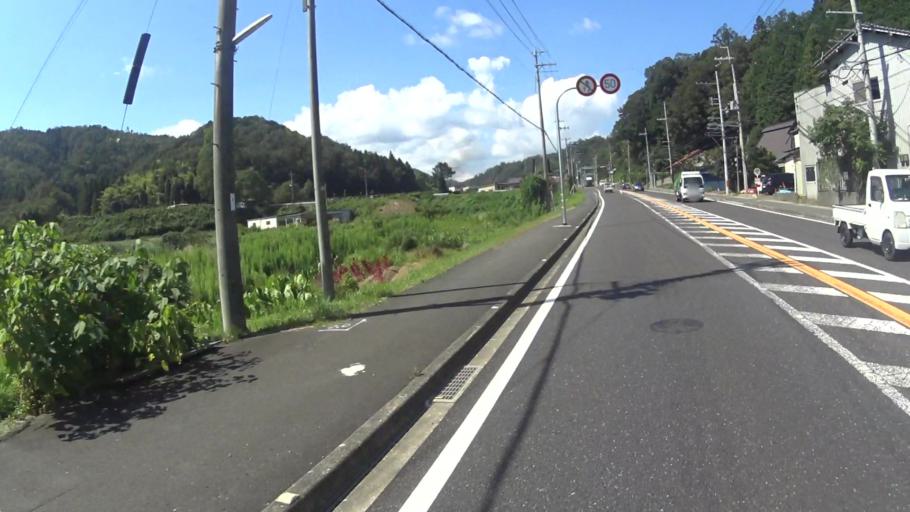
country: JP
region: Kyoto
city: Maizuru
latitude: 35.4470
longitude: 135.2928
